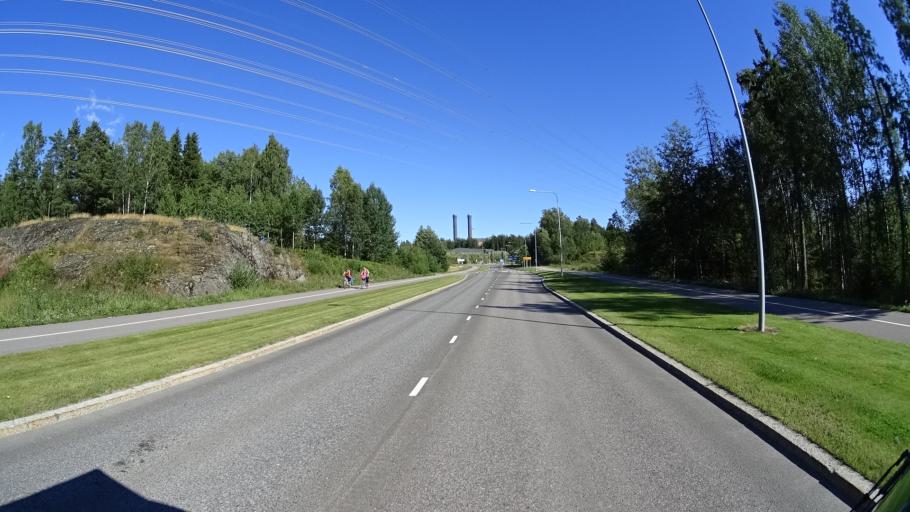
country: FI
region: Uusimaa
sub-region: Helsinki
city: Vantaa
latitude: 60.2211
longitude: 25.1560
